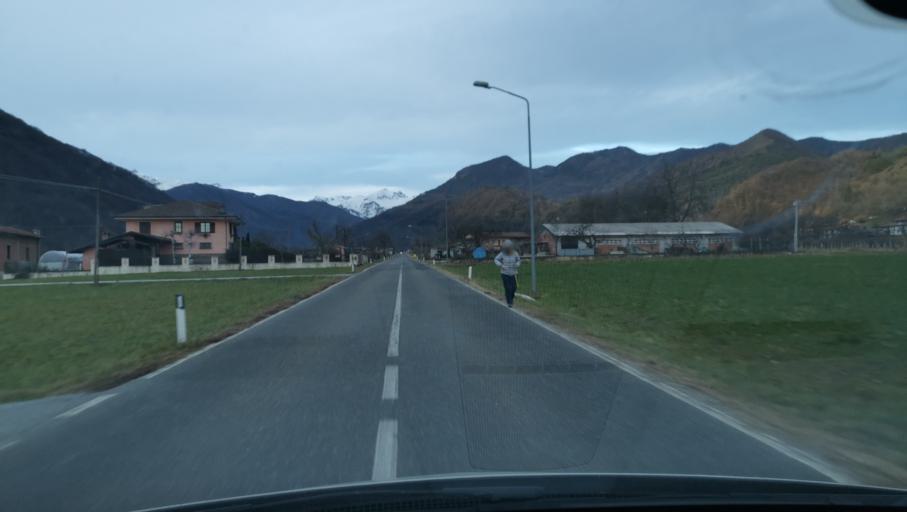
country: IT
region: Piedmont
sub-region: Provincia di Cuneo
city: Valgrana
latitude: 44.4122
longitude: 7.3680
